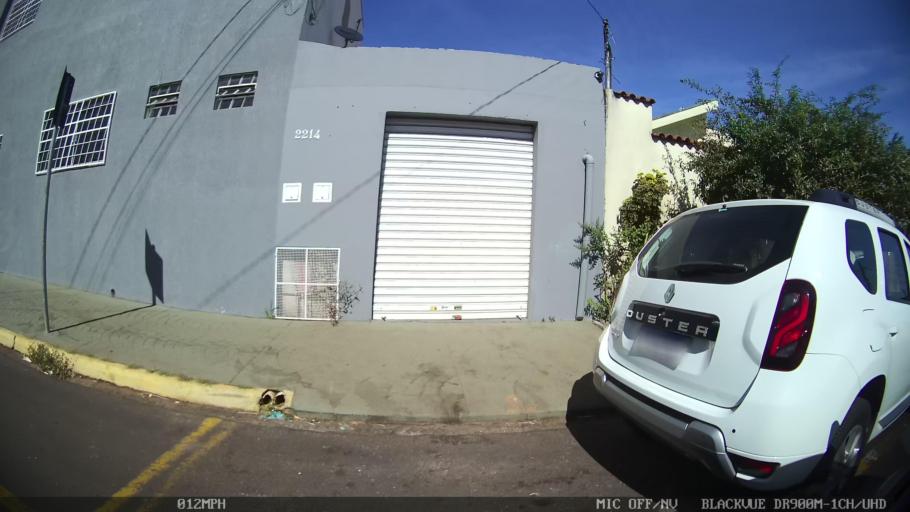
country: BR
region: Sao Paulo
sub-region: Franca
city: Franca
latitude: -20.5274
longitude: -47.3702
